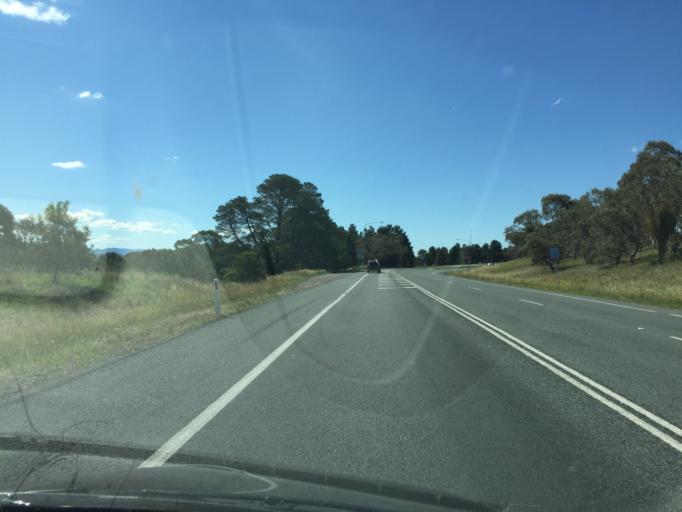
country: AU
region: Australian Capital Territory
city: Macarthur
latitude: -35.4392
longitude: 149.1271
